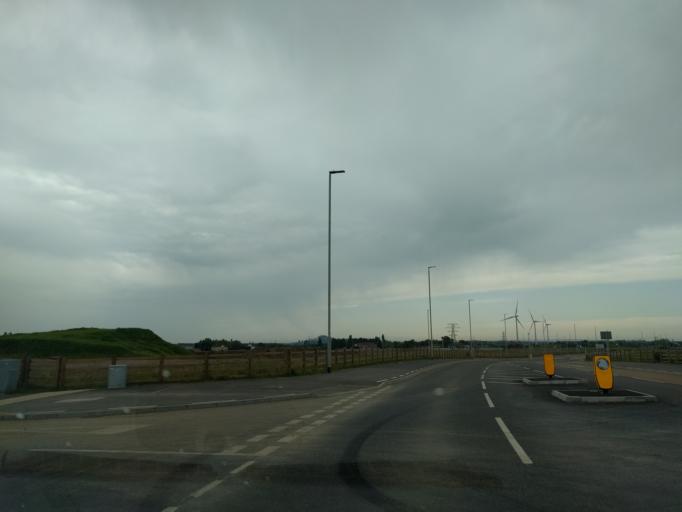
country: GB
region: England
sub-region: Nottinghamshire
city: Newark on Trent
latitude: 53.0556
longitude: -0.8059
